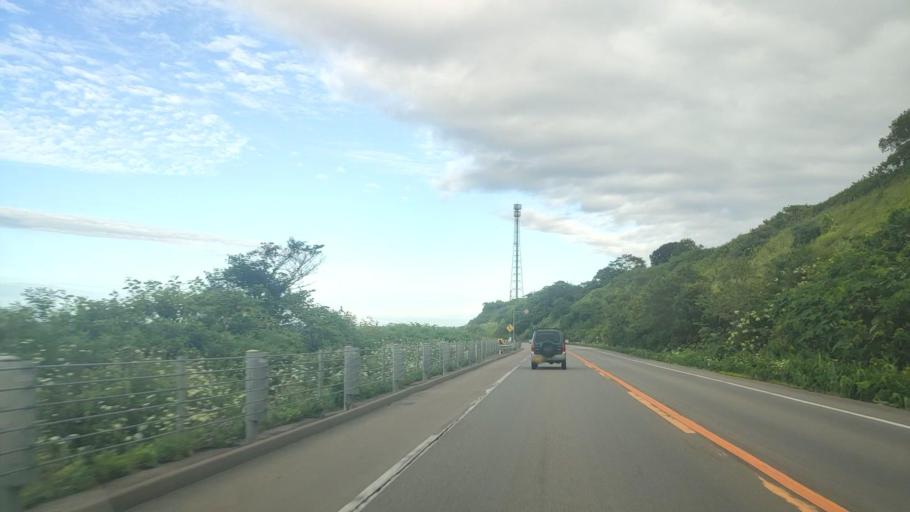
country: JP
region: Hokkaido
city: Nanae
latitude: 42.2000
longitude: 140.4114
